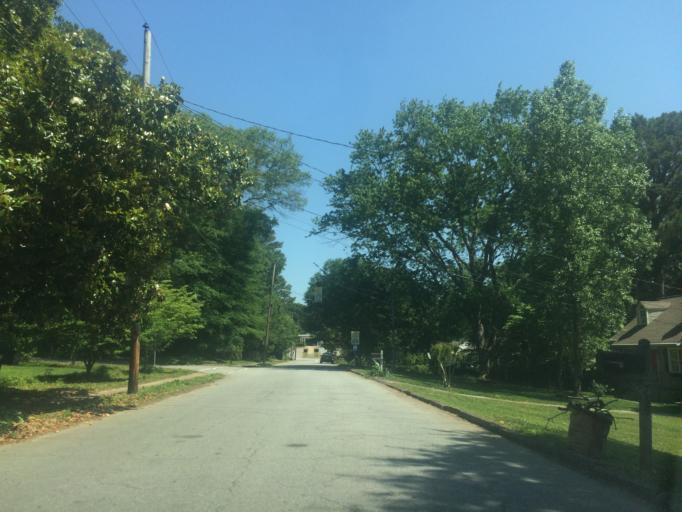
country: US
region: Georgia
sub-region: DeKalb County
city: North Decatur
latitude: 33.8002
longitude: -84.2901
